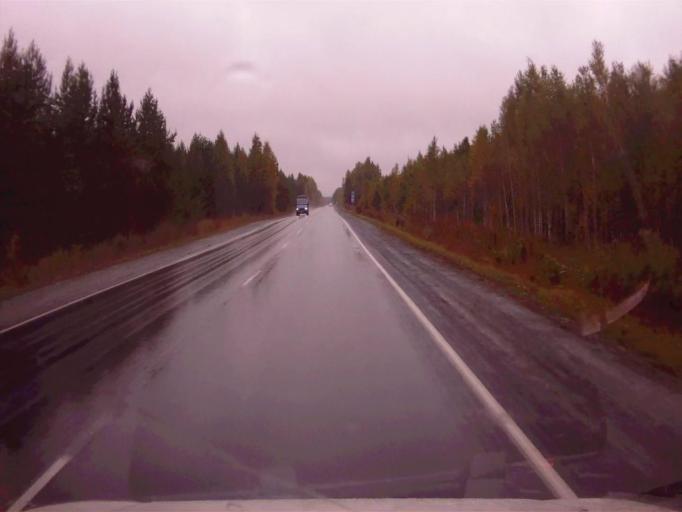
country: RU
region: Chelyabinsk
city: Tayginka
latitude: 55.5395
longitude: 60.6466
